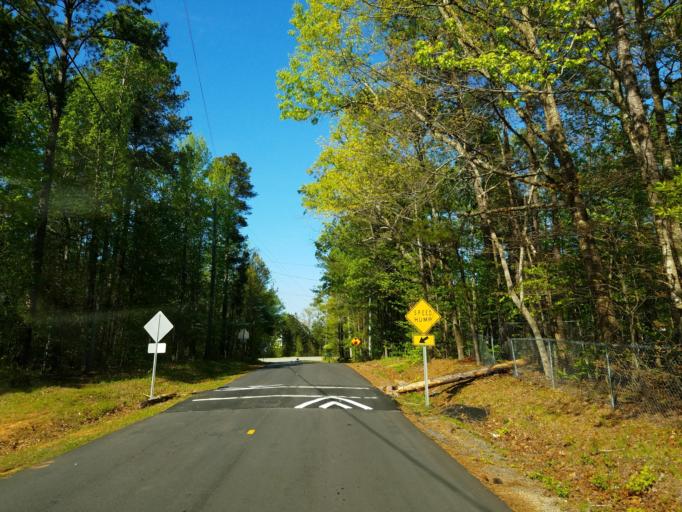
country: US
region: Georgia
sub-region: Douglas County
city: Lithia Springs
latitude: 33.7089
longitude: -84.6487
